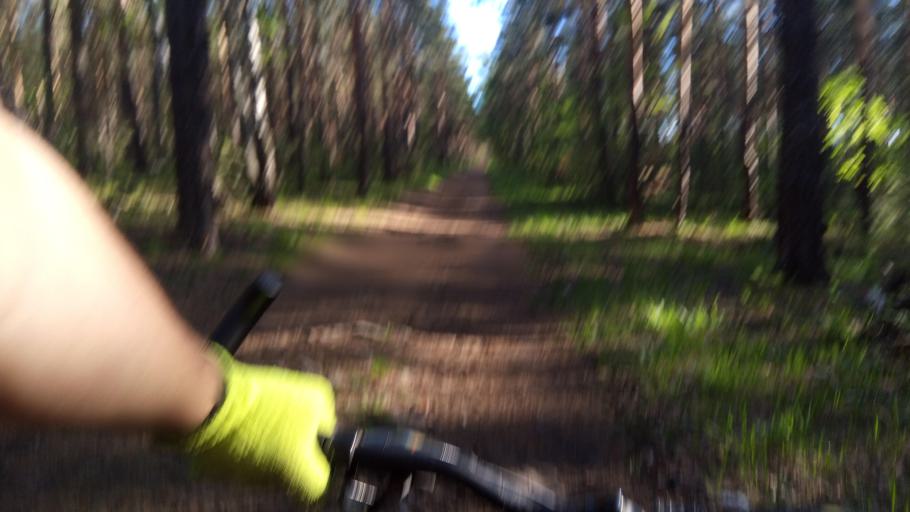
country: RU
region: Chelyabinsk
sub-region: Gorod Chelyabinsk
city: Chelyabinsk
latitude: 55.1366
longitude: 61.3365
